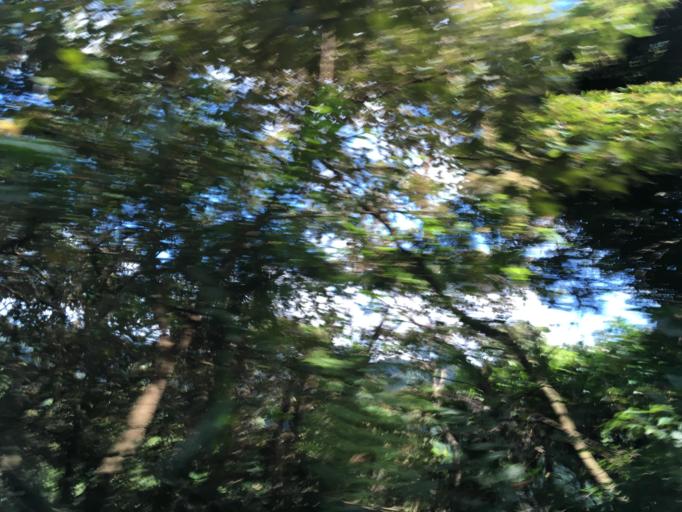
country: TW
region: Taipei
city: Taipei
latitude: 24.9368
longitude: 121.5811
